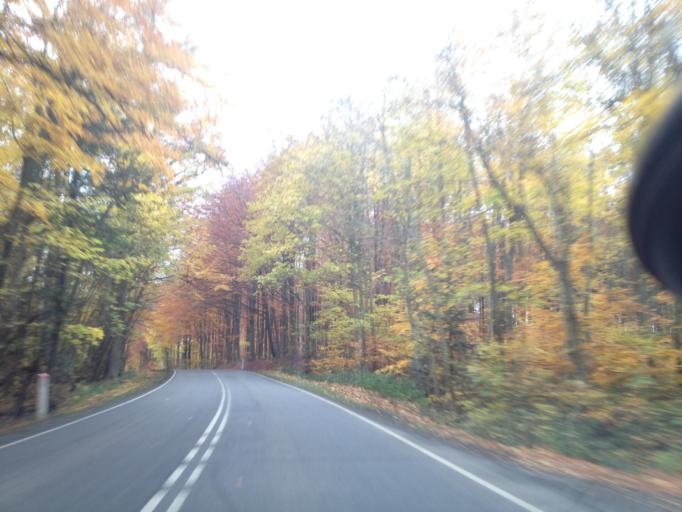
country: DK
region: South Denmark
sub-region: Assens Kommune
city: Vissenbjerg
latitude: 55.4454
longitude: 10.1678
